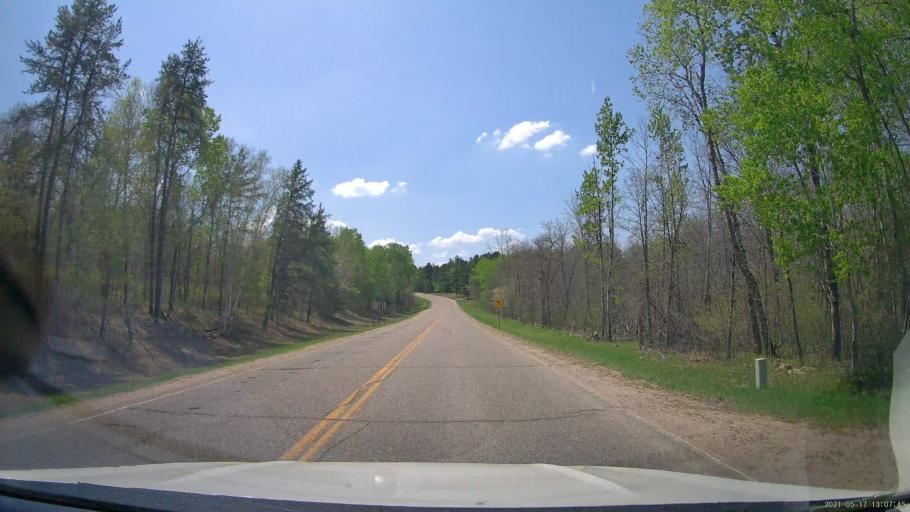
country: US
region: Minnesota
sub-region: Hubbard County
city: Park Rapids
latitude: 47.0456
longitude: -94.9153
